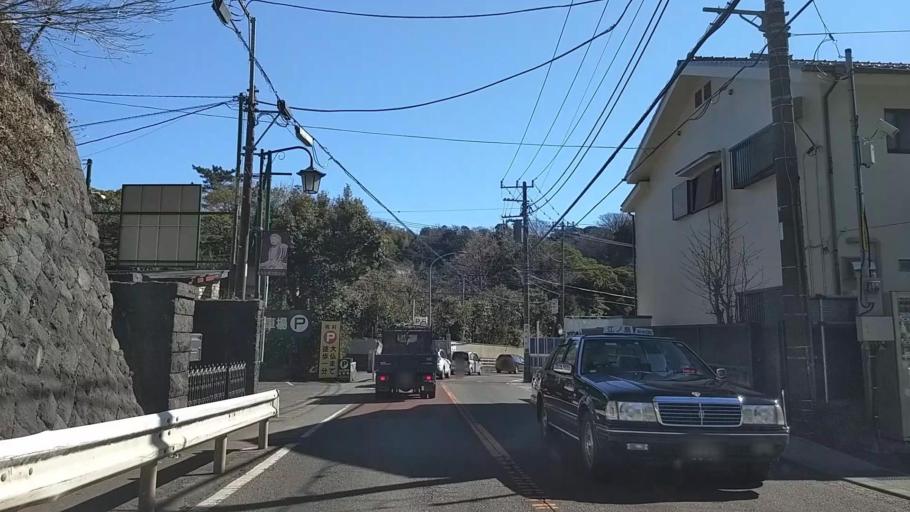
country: JP
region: Kanagawa
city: Kamakura
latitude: 35.3168
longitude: 139.5345
